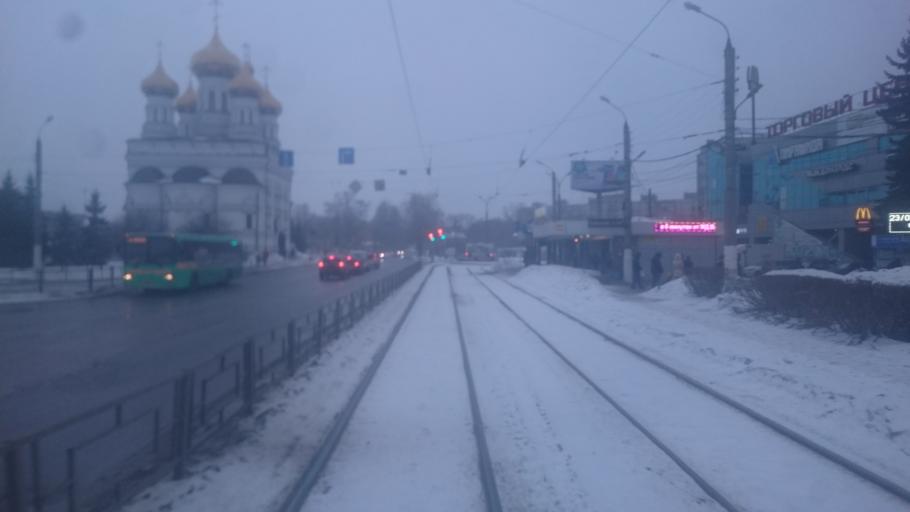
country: RU
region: Tverskaya
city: Tver
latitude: 56.8364
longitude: 35.8949
